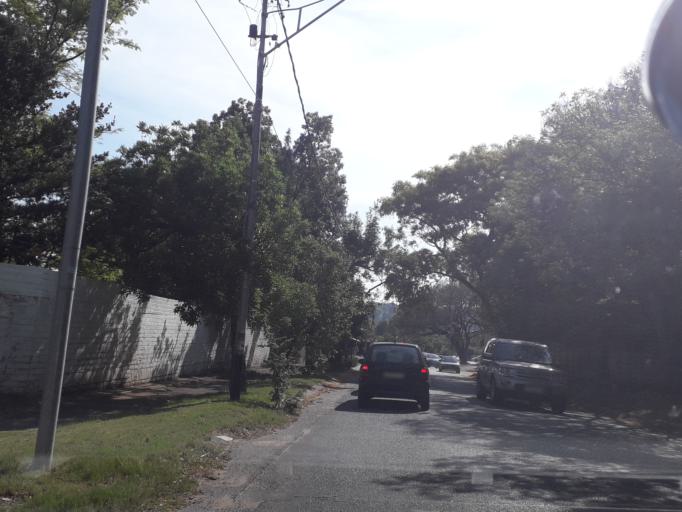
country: ZA
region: Gauteng
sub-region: City of Johannesburg Metropolitan Municipality
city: Johannesburg
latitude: -26.1245
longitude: 28.0297
